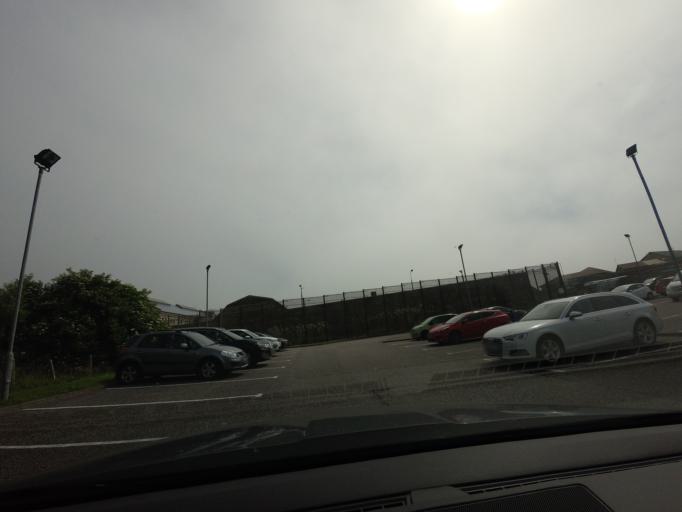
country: GB
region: Scotland
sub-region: Aberdeenshire
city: Peterhead
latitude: 57.4923
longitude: -1.7932
